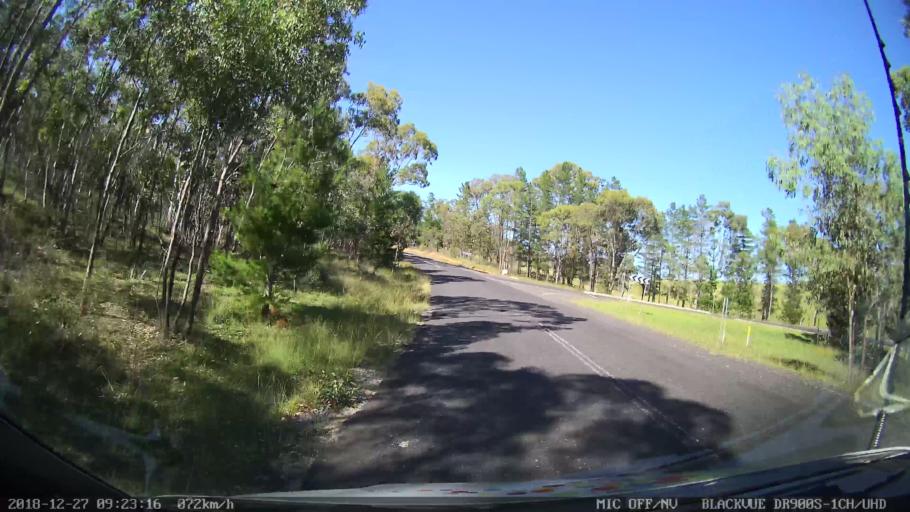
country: AU
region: New South Wales
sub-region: Lithgow
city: Portland
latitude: -33.1245
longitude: 149.9987
